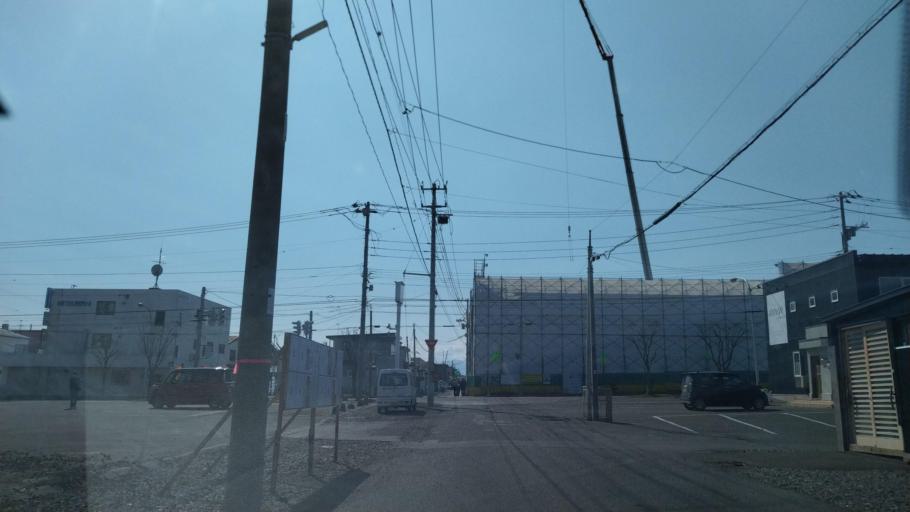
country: JP
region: Hokkaido
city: Obihiro
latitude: 42.8942
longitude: 143.2018
